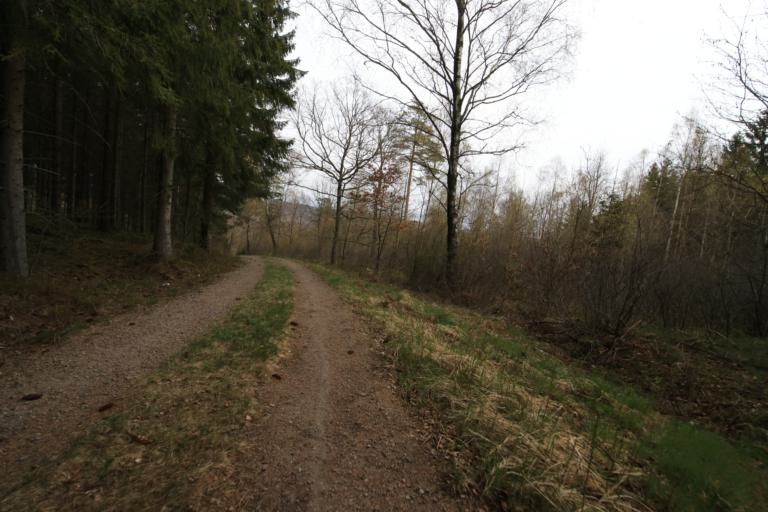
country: SE
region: Halland
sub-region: Varbergs Kommun
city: Tvaaker
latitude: 57.1520
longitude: 12.4597
